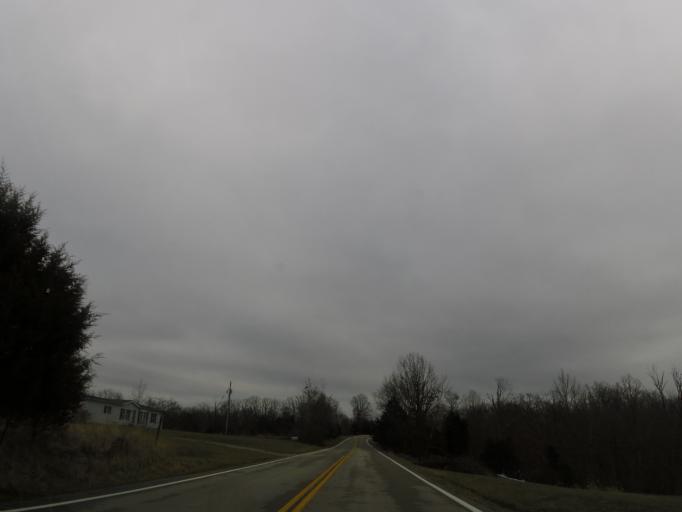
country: US
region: Kentucky
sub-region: Franklin County
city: Frankfort
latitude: 38.3422
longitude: -84.9775
